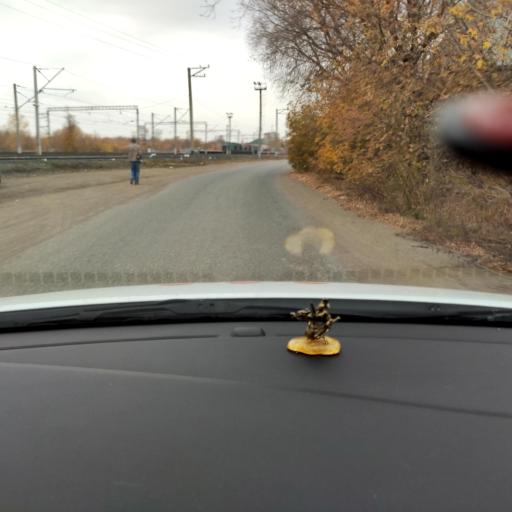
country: RU
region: Tatarstan
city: Staroye Arakchino
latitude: 55.8018
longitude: 49.0163
